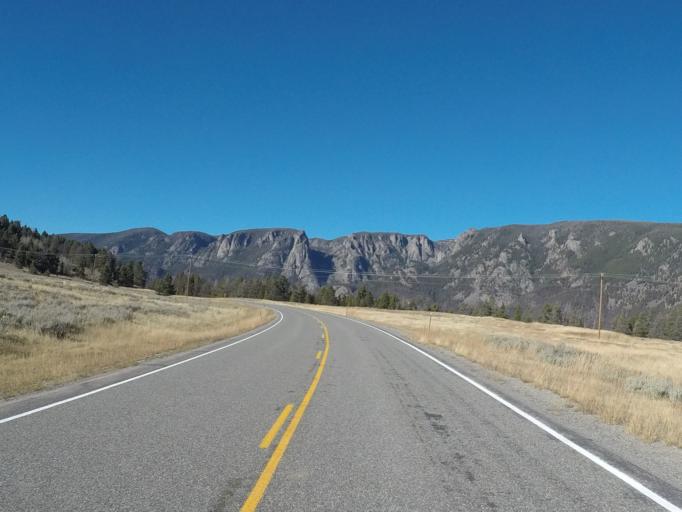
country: US
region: Montana
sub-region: Carbon County
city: Red Lodge
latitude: 44.8413
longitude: -109.4980
